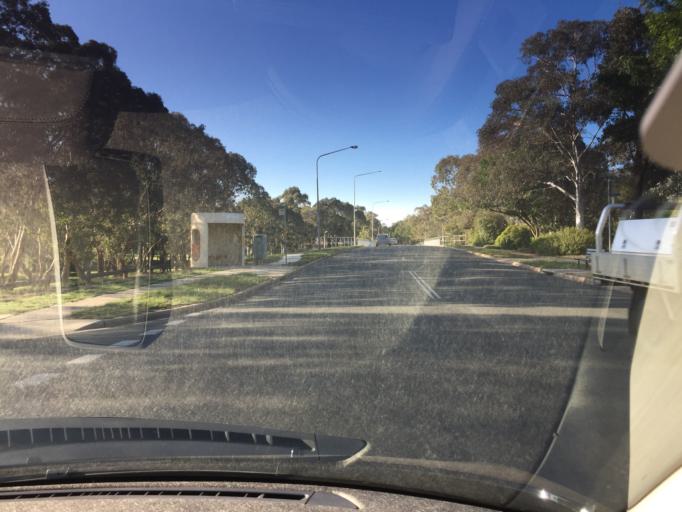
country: AU
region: Australian Capital Territory
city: Kaleen
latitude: -35.2209
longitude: 149.1113
